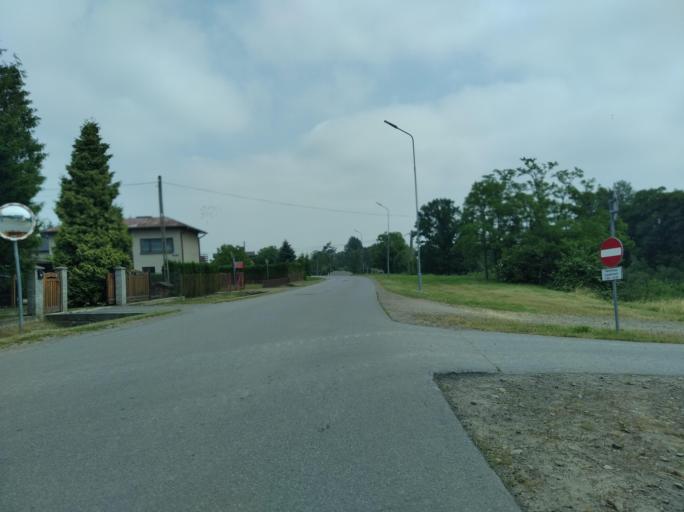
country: PL
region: Subcarpathian Voivodeship
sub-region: Powiat sanocki
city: Besko
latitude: 49.5929
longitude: 21.9591
